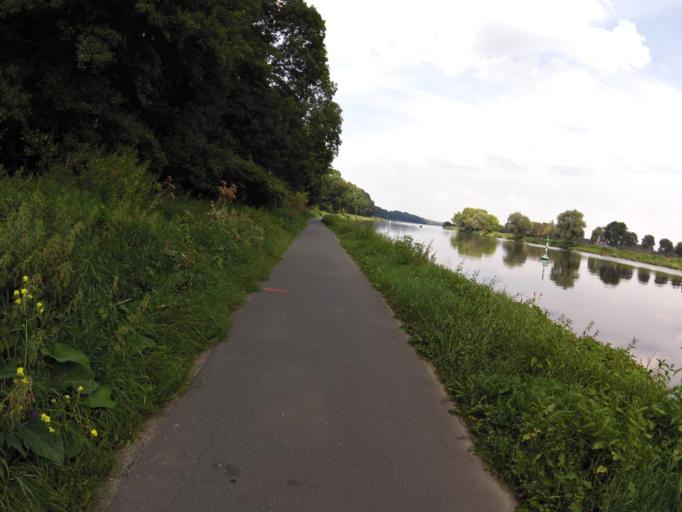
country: DE
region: North Rhine-Westphalia
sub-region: Regierungsbezirk Detmold
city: Minden
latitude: 52.3192
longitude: 8.9219
